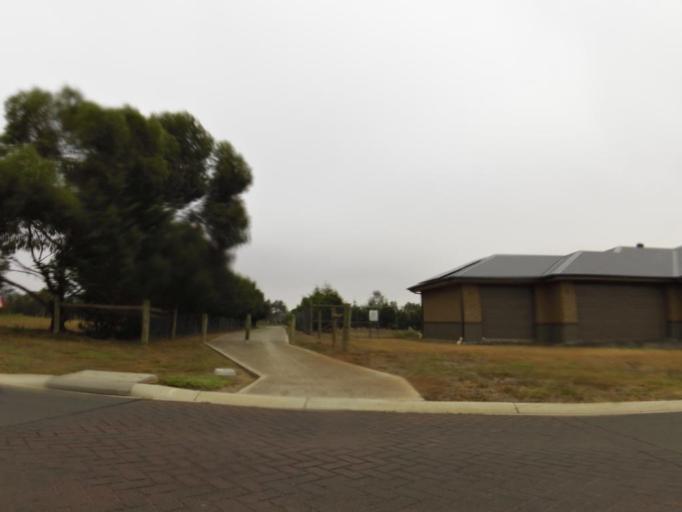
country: AU
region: Victoria
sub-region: Melton
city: Kurunjang
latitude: -37.6791
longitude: 144.6029
